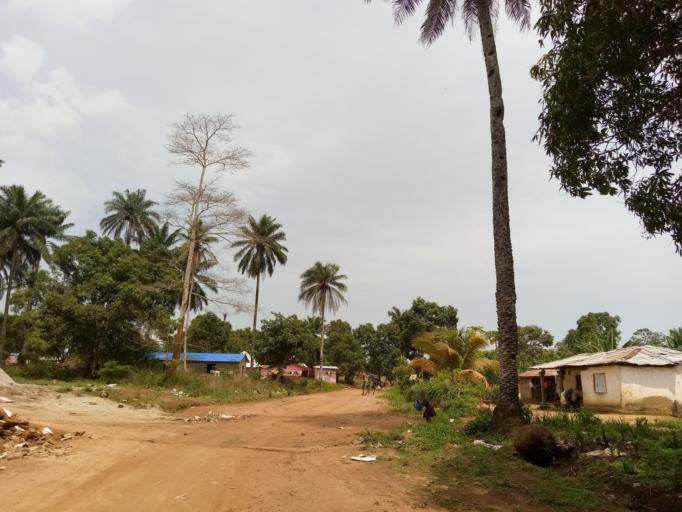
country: SL
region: Western Area
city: Waterloo
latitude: 8.3290
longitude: -13.0150
